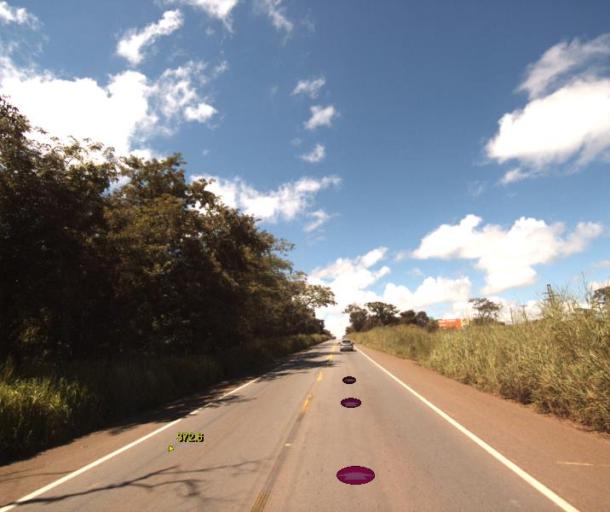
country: BR
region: Goias
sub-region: Jaragua
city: Jaragua
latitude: -15.8420
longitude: -49.2716
